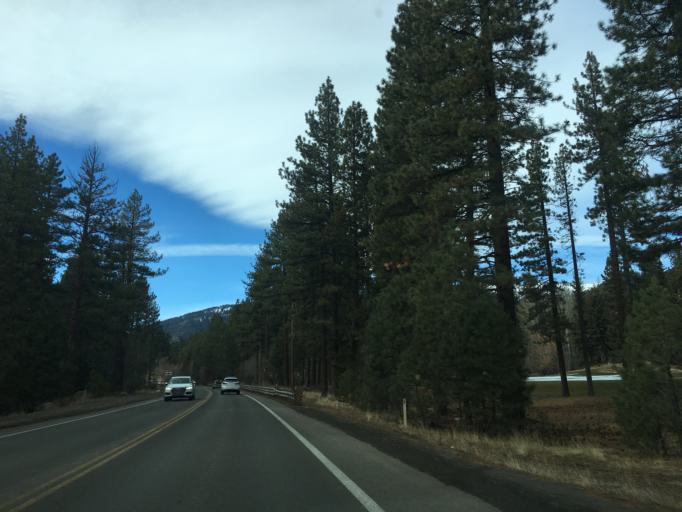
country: US
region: Nevada
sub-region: Washoe County
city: Incline Village
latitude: 39.2479
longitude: -119.9419
